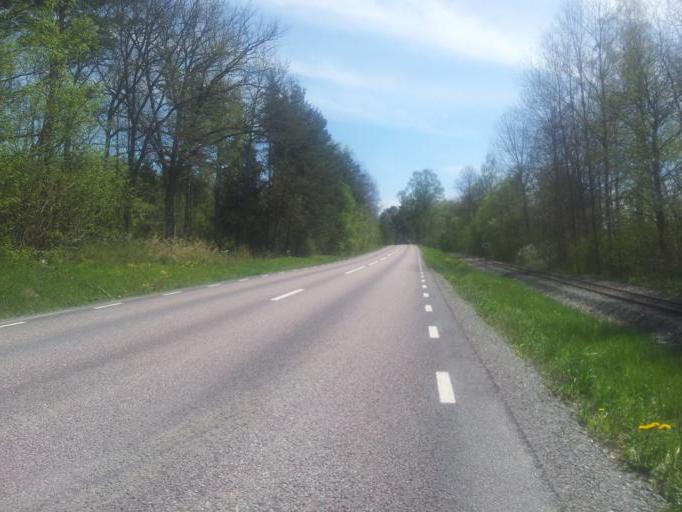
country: SE
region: Uppsala
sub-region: Knivsta Kommun
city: Knivsta
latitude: 59.8810
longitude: 17.9950
